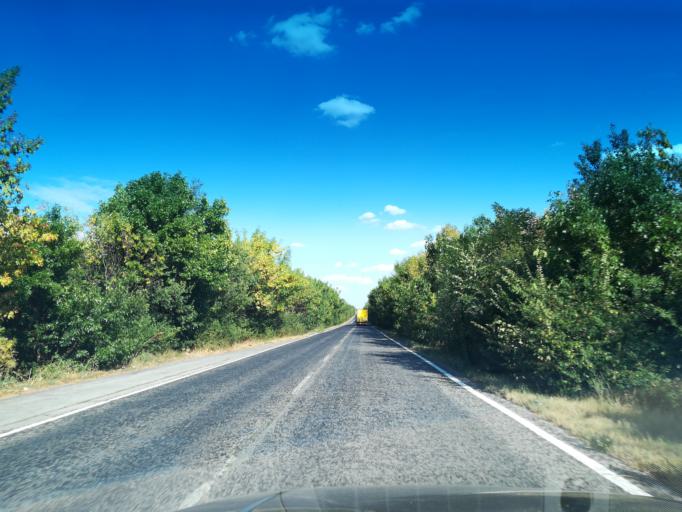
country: BG
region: Khaskovo
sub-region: Obshtina Mineralni Bani
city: Mineralni Bani
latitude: 42.0544
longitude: 25.3101
